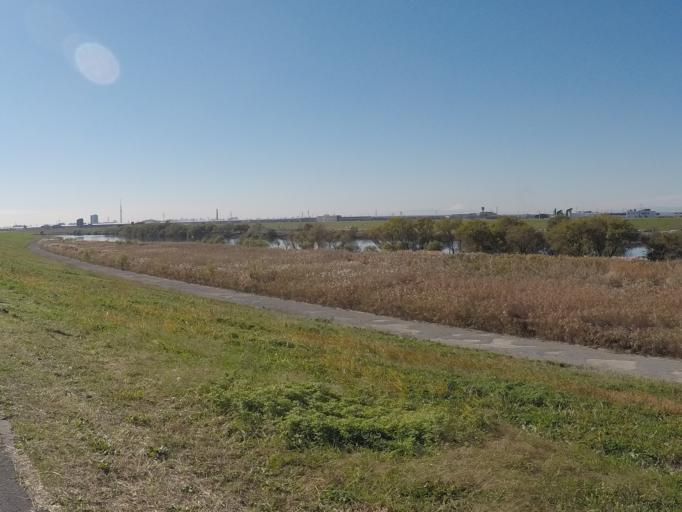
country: JP
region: Chiba
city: Matsudo
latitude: 35.8147
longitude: 139.8934
